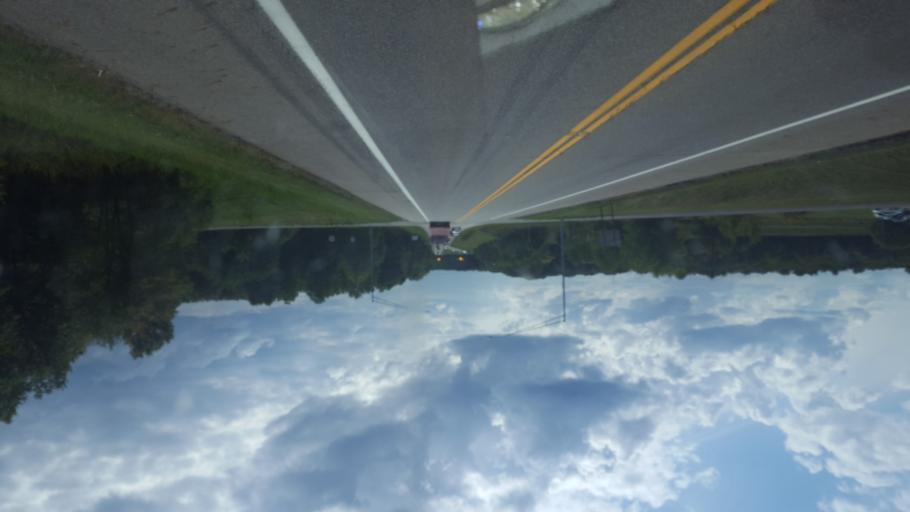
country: US
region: Ohio
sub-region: Portage County
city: Ravenna
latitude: 41.1240
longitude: -81.2360
